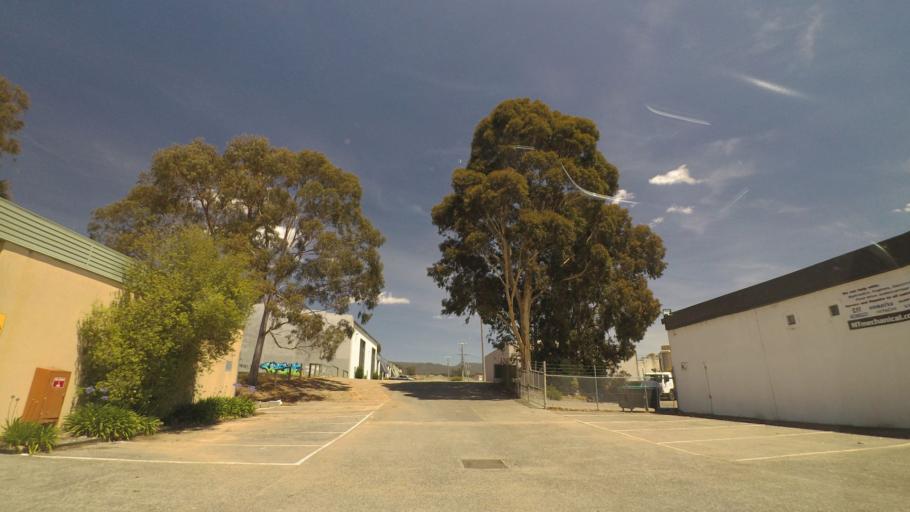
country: AU
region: Victoria
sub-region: Maroondah
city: Kilsyth South
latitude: -37.8148
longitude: 145.3225
